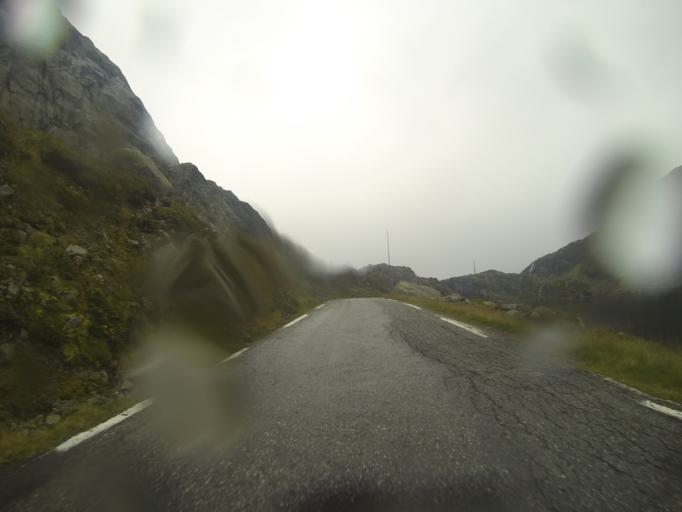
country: NO
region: Hordaland
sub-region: Odda
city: Odda
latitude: 59.7745
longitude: 6.7433
